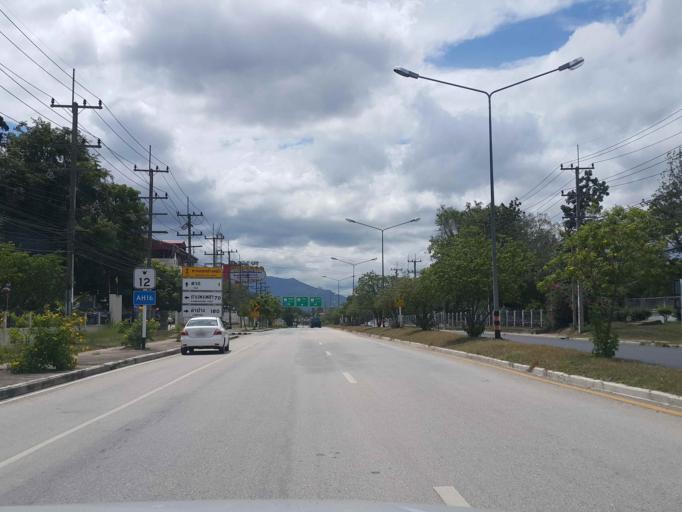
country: TH
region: Tak
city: Tak
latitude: 16.8838
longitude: 99.1319
